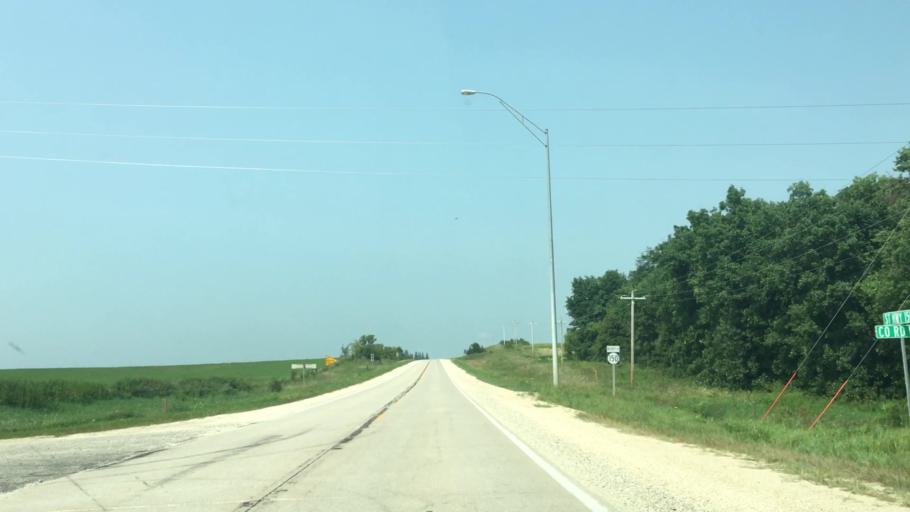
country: US
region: Iowa
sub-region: Fayette County
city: West Union
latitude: 43.1292
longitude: -91.8691
